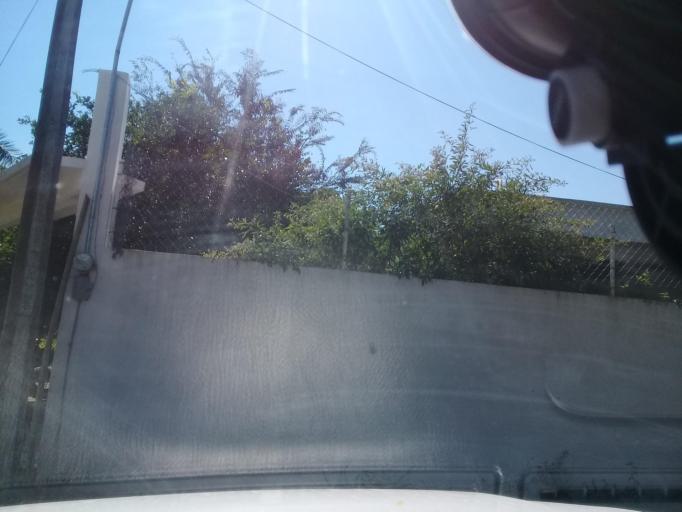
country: MX
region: Hidalgo
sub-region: Huejutla de Reyes
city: Parque de Poblamiento Solidaridad
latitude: 21.1593
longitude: -98.4057
